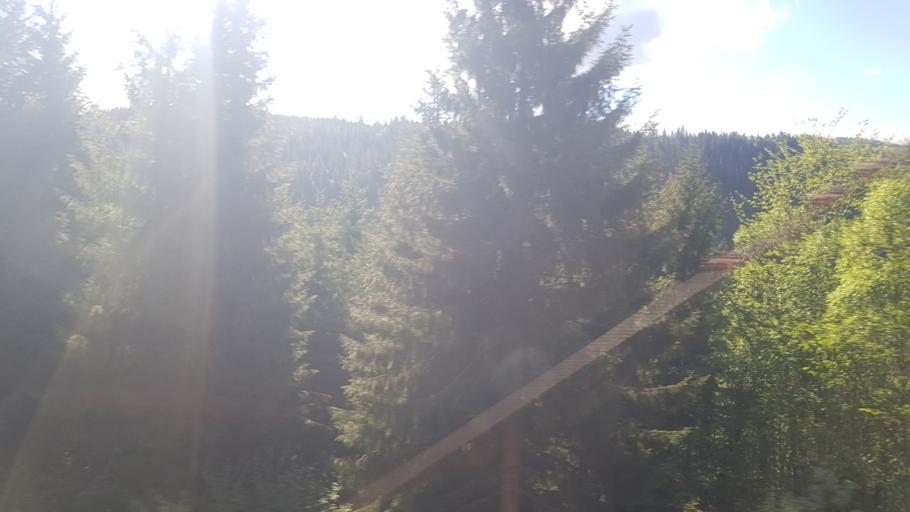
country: NO
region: Sor-Trondelag
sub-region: Midtre Gauldal
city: Storen
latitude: 62.9767
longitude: 10.2184
